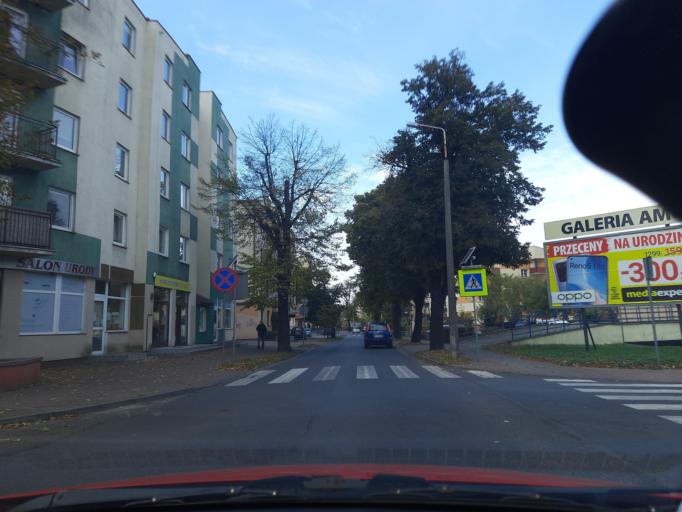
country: PL
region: Kujawsko-Pomorskie
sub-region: Torun
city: Torun
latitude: 53.0241
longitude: 18.6066
